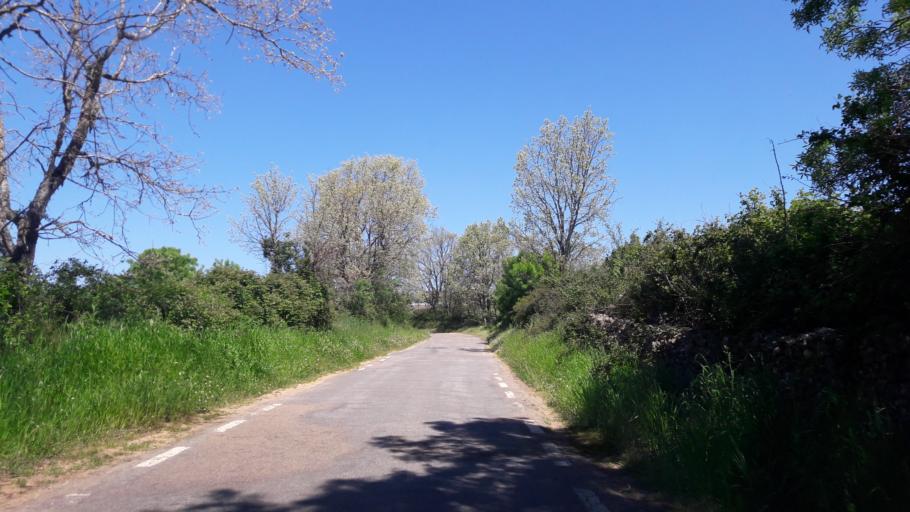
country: ES
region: Castille and Leon
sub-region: Provincia de Salamanca
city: Endrinal
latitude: 40.5765
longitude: -5.8062
